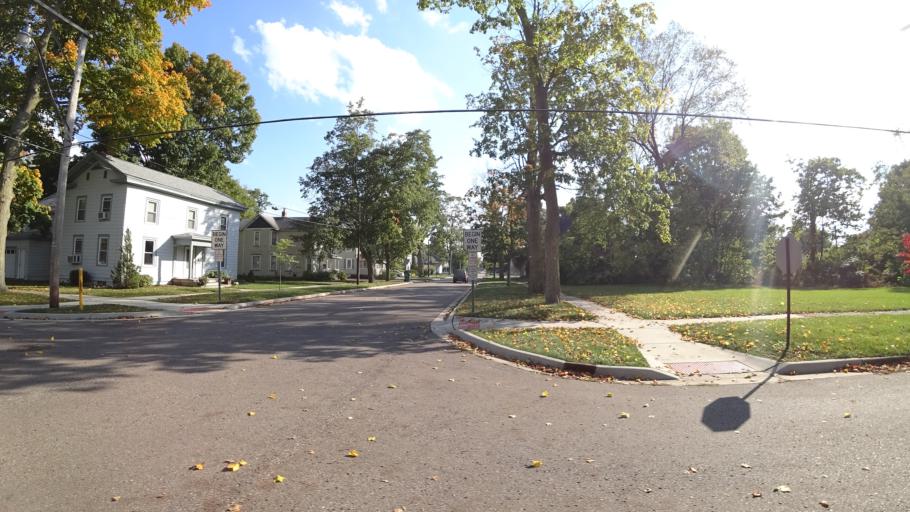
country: US
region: Michigan
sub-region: Saint Joseph County
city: Three Rivers
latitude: 41.9525
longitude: -85.6333
